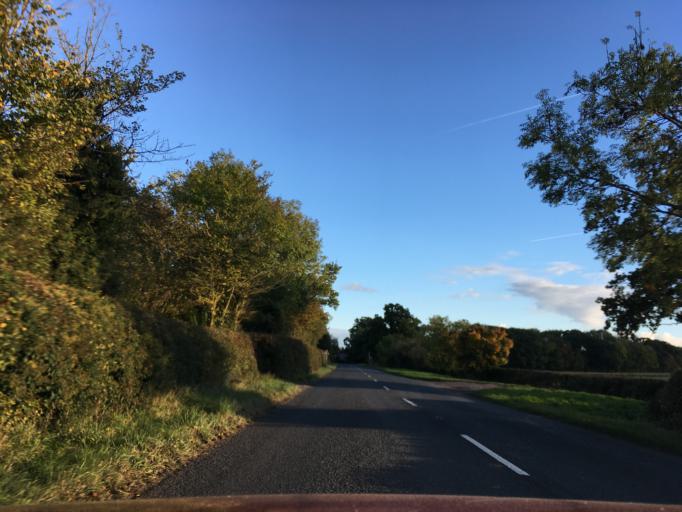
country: GB
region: England
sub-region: Worcestershire
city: Upton upon Severn
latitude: 52.0008
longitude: -2.2343
